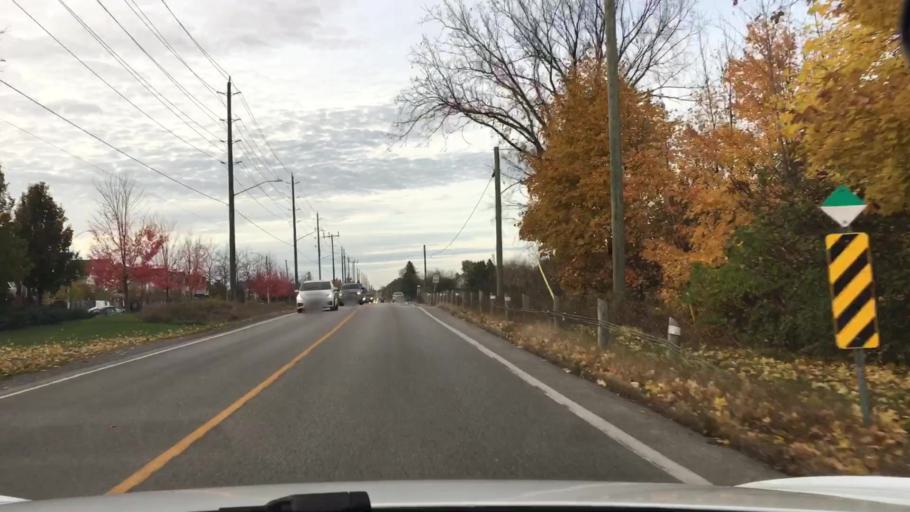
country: CA
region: Ontario
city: Oshawa
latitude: 43.9373
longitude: -78.8268
